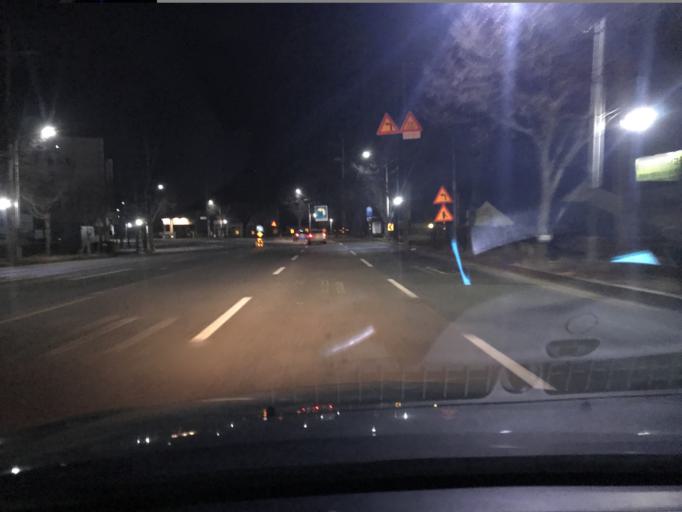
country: KR
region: Daegu
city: Hwawon
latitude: 35.6947
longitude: 128.4391
